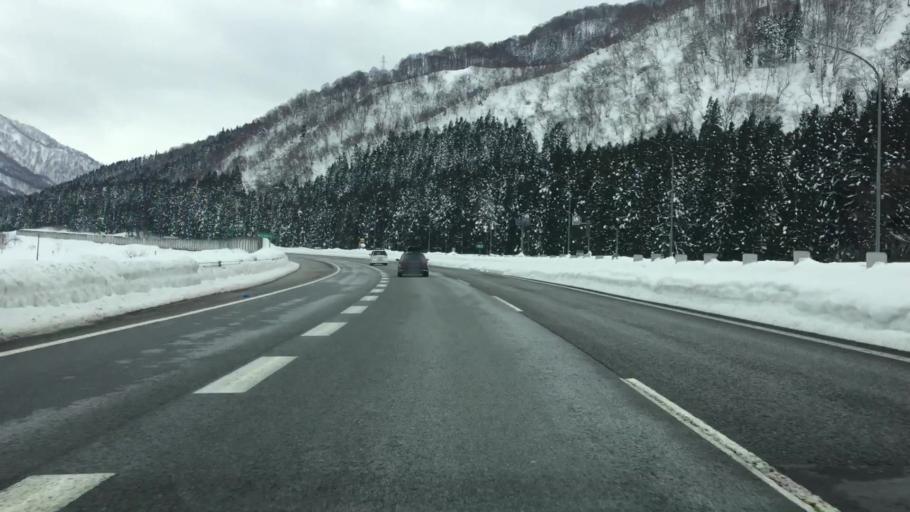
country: JP
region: Niigata
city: Shiozawa
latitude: 36.8966
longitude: 138.8454
